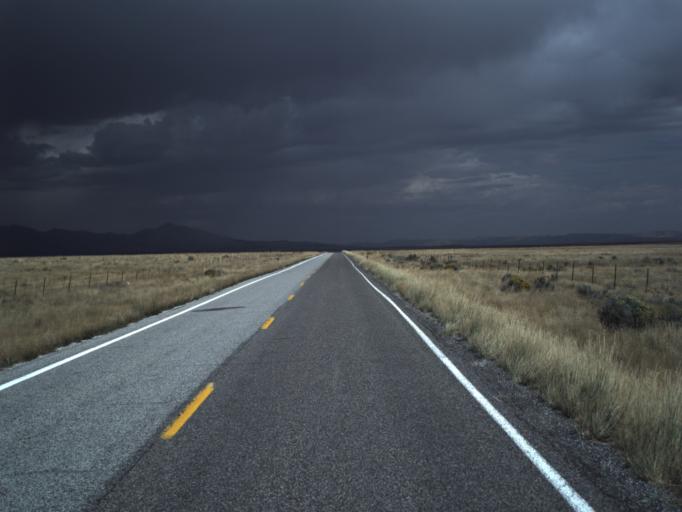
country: US
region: Idaho
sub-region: Oneida County
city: Malad City
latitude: 41.8793
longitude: -113.1183
